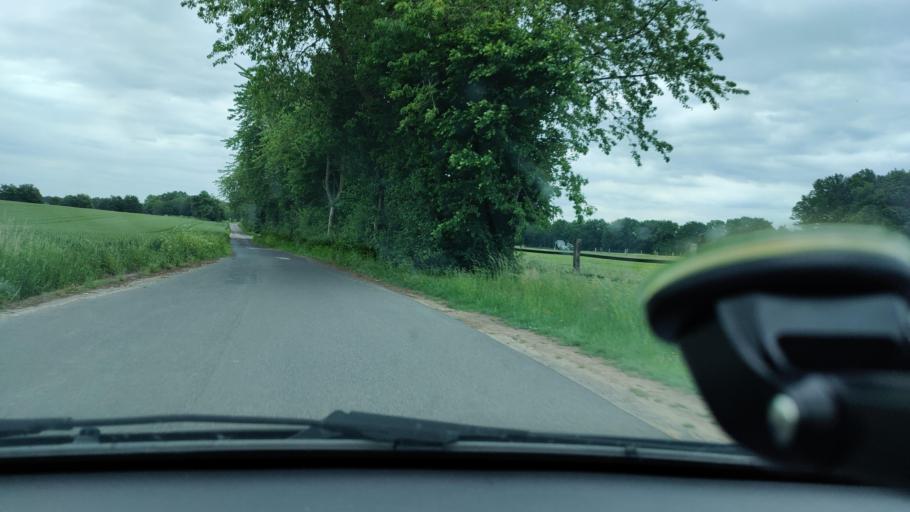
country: DE
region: North Rhine-Westphalia
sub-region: Regierungsbezirk Dusseldorf
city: Goch
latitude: 51.7096
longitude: 6.1331
